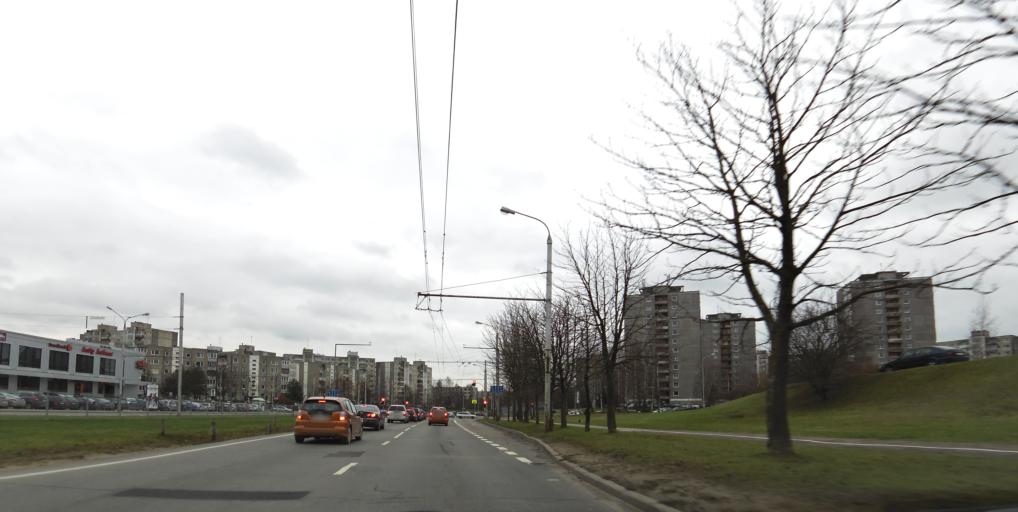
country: LT
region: Vilnius County
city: Justiniskes
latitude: 54.7084
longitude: 25.2262
